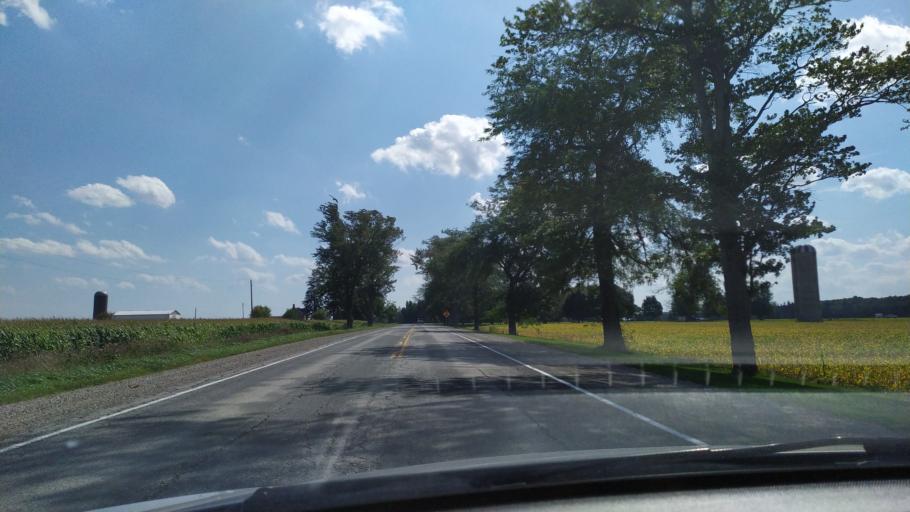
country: CA
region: Ontario
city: Stratford
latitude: 43.3205
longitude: -80.9870
